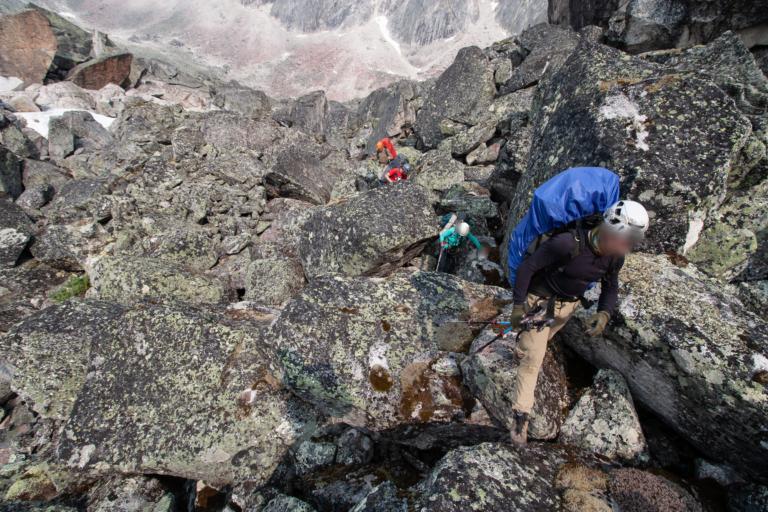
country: RU
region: Respublika Buryatiya
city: Novyy Uoyan
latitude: 56.2206
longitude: 110.9919
